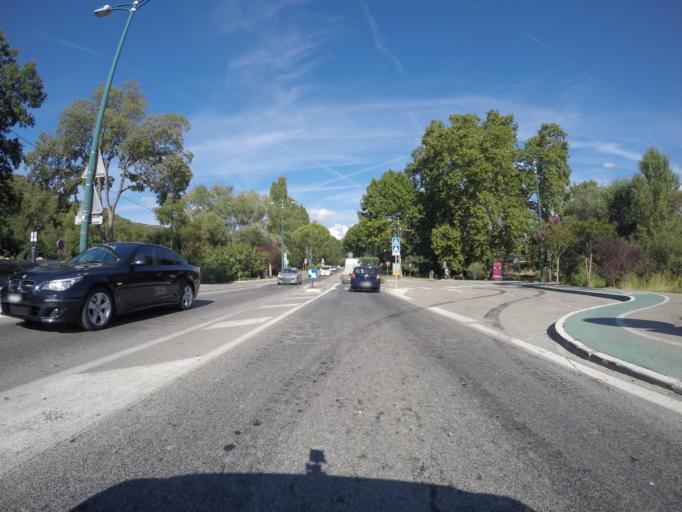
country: FR
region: Provence-Alpes-Cote d'Azur
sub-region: Departement des Alpes-Maritimes
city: Villeneuve-Loubet
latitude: 43.6563
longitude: 7.1214
